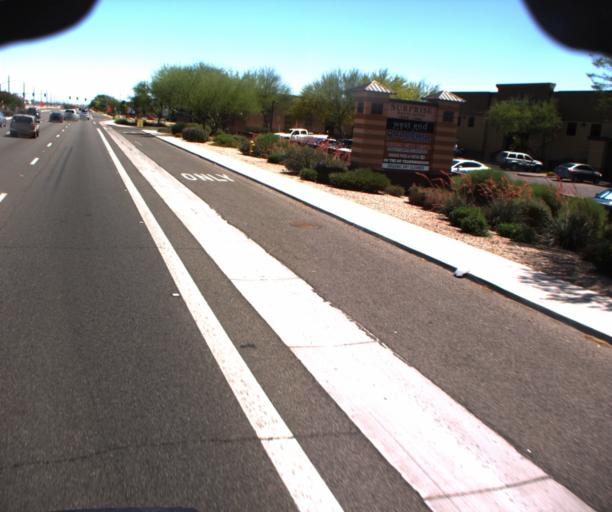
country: US
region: Arizona
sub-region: Maricopa County
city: Sun City West
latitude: 33.6510
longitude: -112.3663
